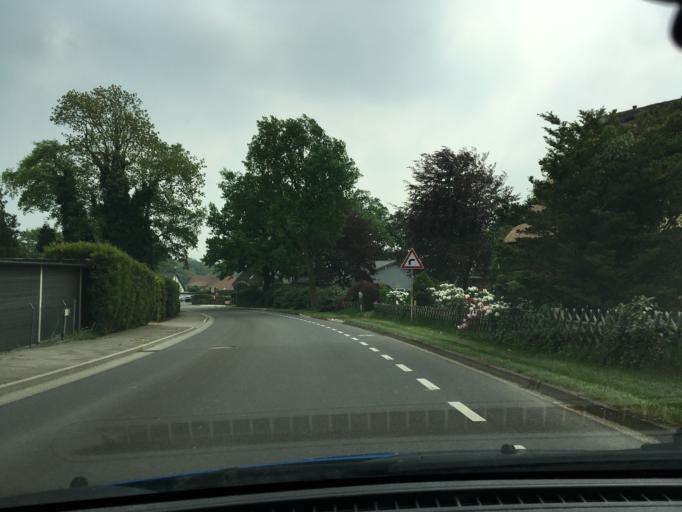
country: DE
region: Lower Saxony
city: Seevetal
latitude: 53.4087
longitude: 9.8965
